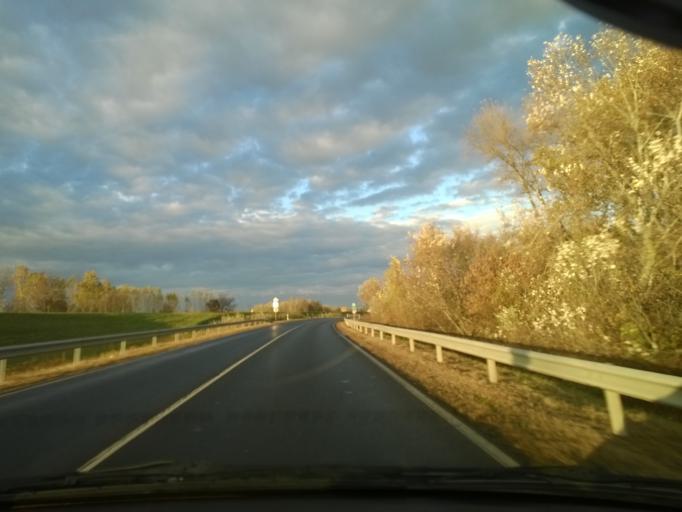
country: HU
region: Bacs-Kiskun
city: Harta
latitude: 46.6841
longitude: 19.0163
